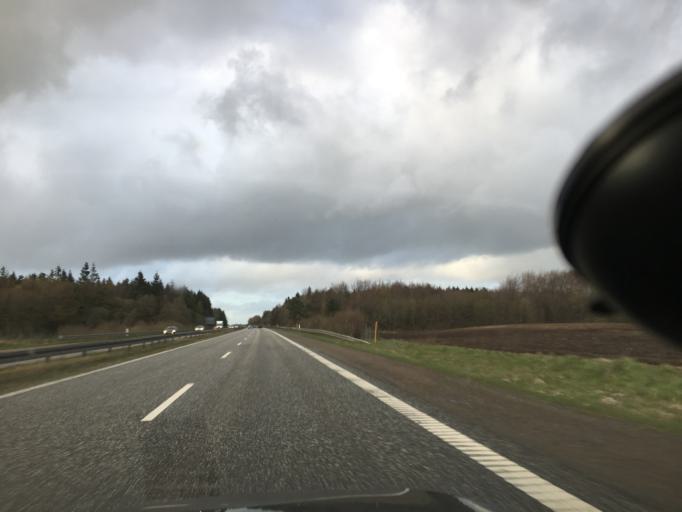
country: DK
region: North Denmark
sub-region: Mariagerfjord Kommune
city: Hobro
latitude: 56.6351
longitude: 9.7356
